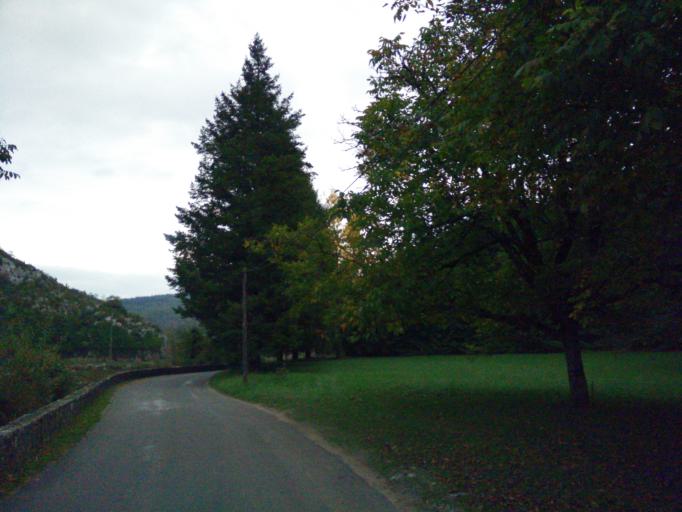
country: FR
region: Midi-Pyrenees
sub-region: Departement du Lot
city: Cajarc
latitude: 44.5098
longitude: 1.6492
